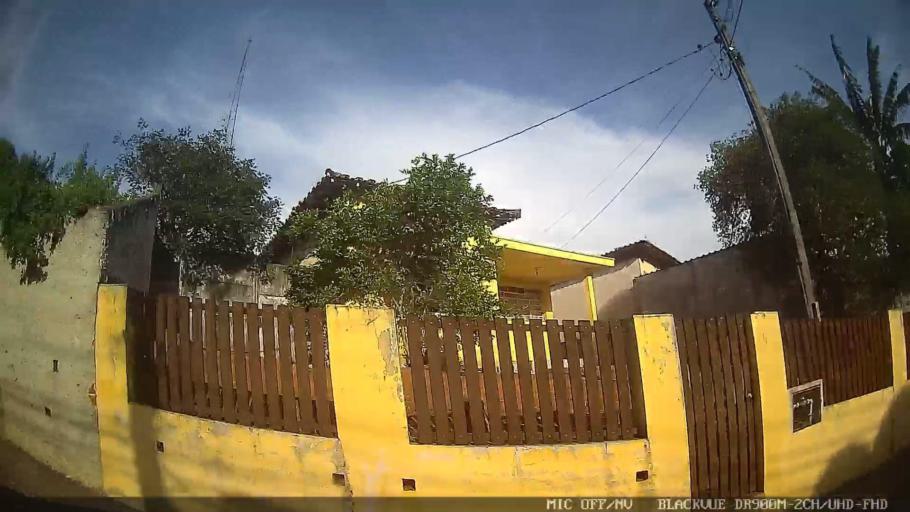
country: BR
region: Sao Paulo
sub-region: Tiete
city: Tiete
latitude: -23.0937
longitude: -47.7180
